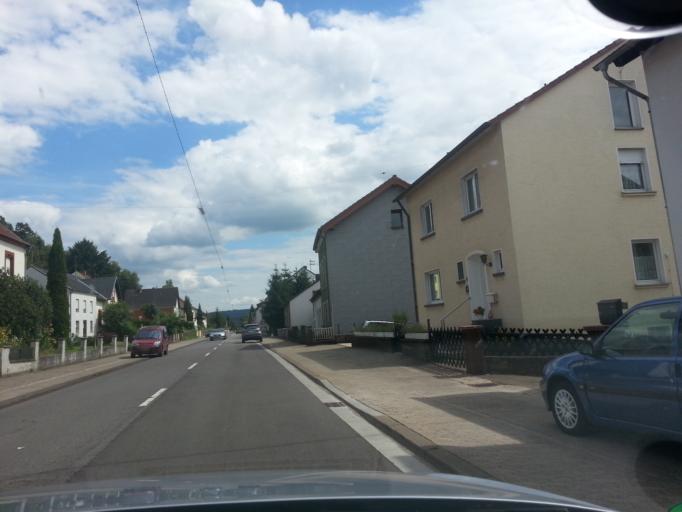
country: DE
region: Saarland
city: Mettlach
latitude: 49.4718
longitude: 6.6110
